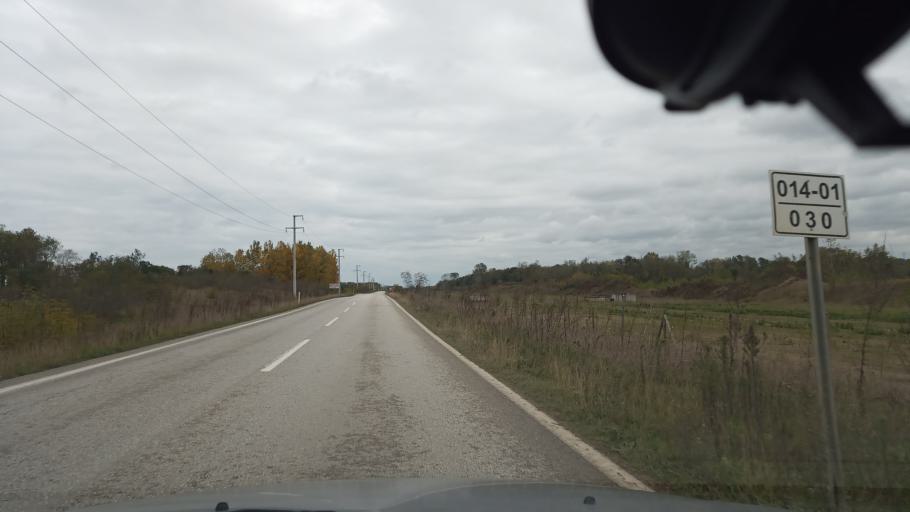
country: TR
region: Sakarya
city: Karasu
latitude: 41.1214
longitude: 30.5808
